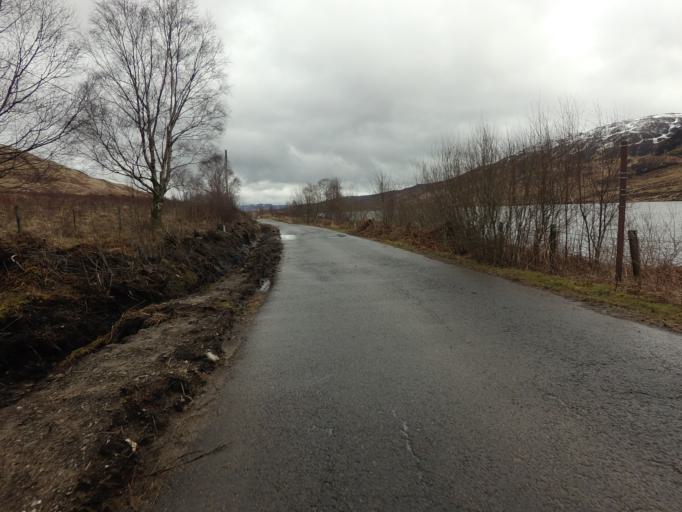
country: GB
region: Scotland
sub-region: West Dunbartonshire
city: Balloch
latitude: 56.2482
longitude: -4.6365
